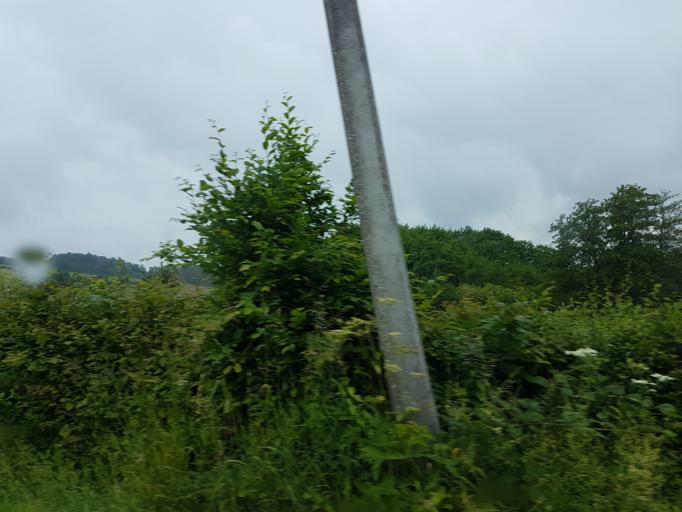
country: FR
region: Bourgogne
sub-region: Departement de la Nievre
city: Chateau-Chinon(Ville)
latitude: 47.1619
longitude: 3.8550
